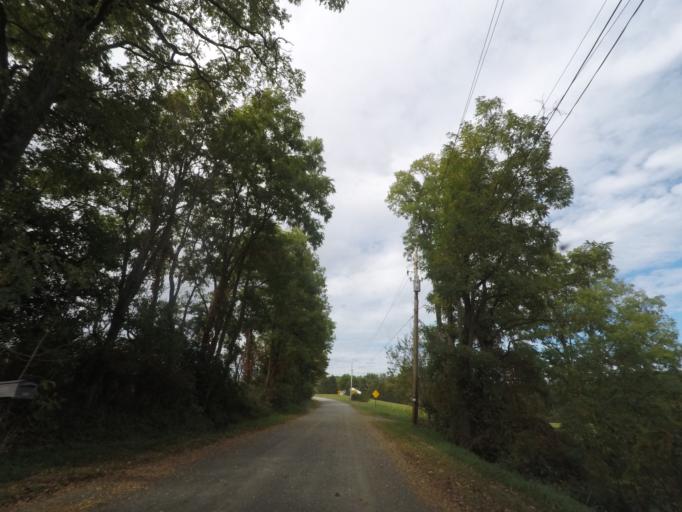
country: US
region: New York
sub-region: Rensselaer County
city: West Sand Lake
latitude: 42.5829
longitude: -73.6128
